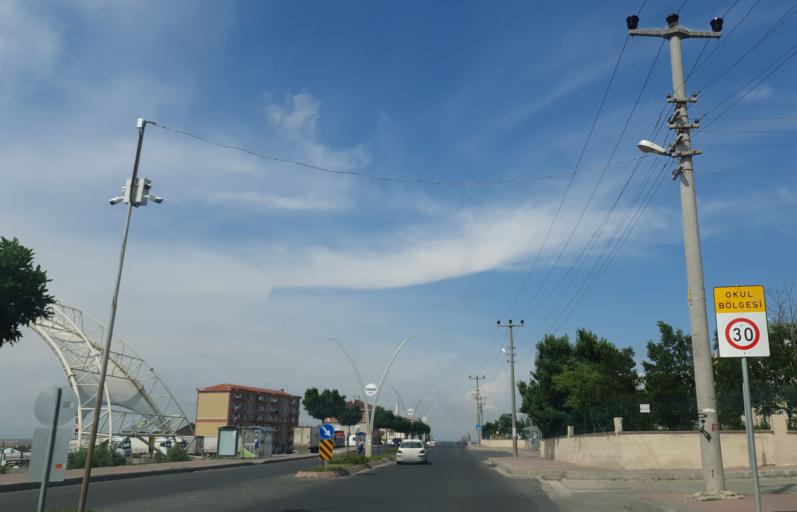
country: TR
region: Tekirdag
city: Marmaracik
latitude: 41.2392
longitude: 27.7115
